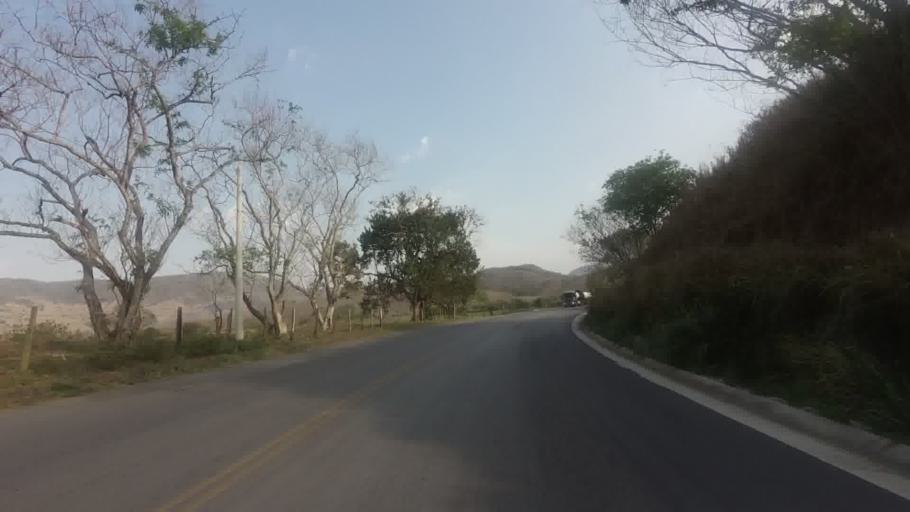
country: BR
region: Rio de Janeiro
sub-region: Cambuci
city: Cambuci
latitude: -21.4029
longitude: -41.9754
